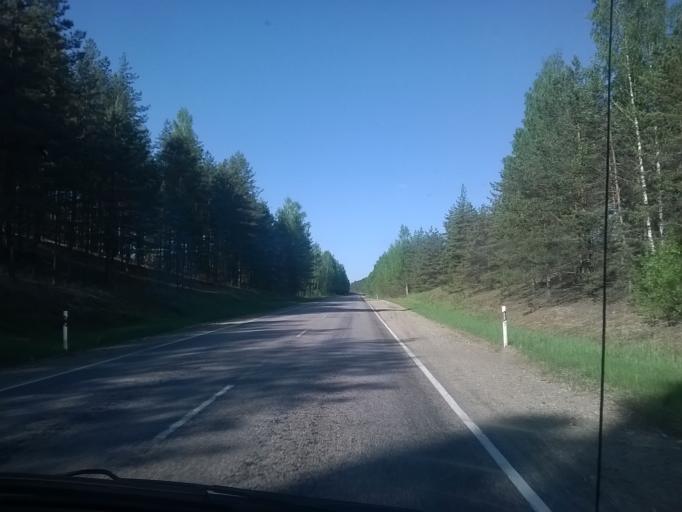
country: LV
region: Strenci
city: Seda
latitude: 57.6331
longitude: 25.8177
